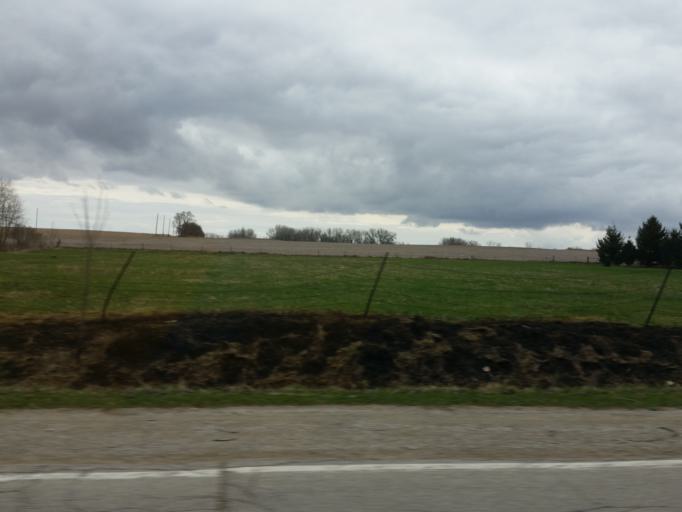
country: US
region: Iowa
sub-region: Benton County
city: Vinton
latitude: 42.3143
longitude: -91.9968
